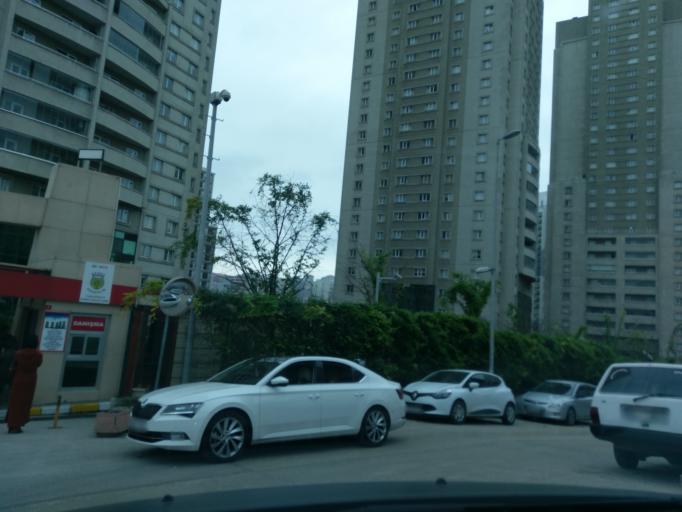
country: TR
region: Istanbul
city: Esenyurt
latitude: 41.0147
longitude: 28.6783
